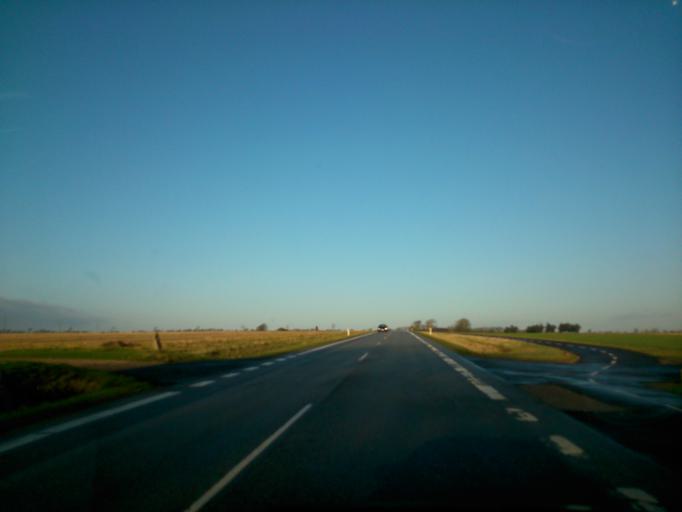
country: DK
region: Central Jutland
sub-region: Ringkobing-Skjern Kommune
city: Videbaek
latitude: 55.9911
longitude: 8.5955
